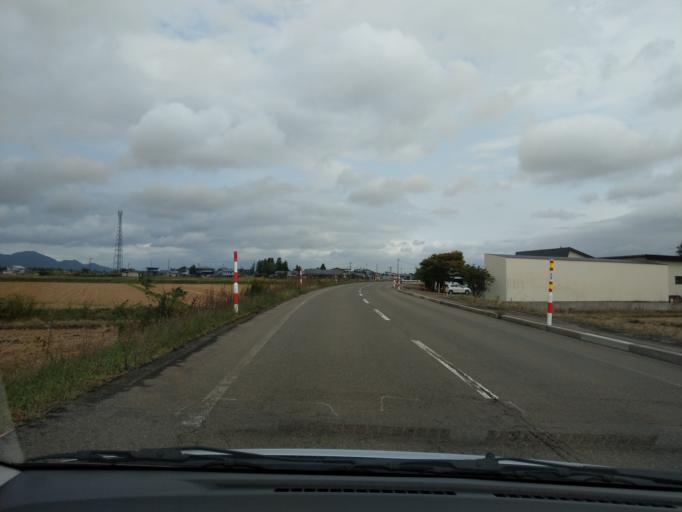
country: JP
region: Akita
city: Omagari
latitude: 39.3790
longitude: 140.4855
